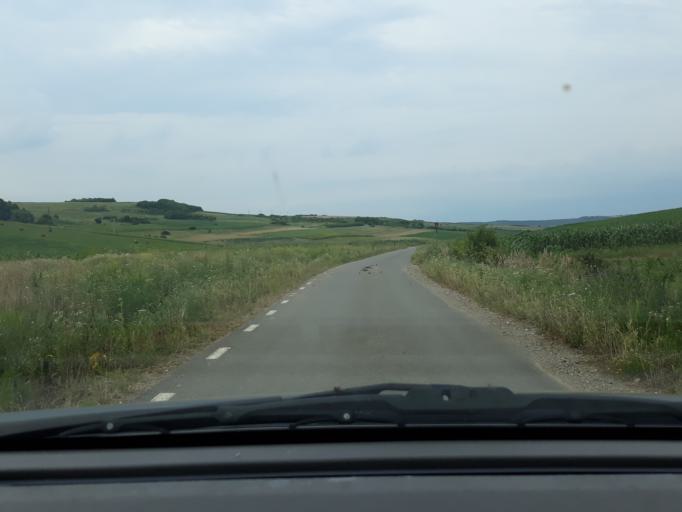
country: RO
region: Salaj
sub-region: Comuna Dobrin
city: Dobrin
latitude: 47.2845
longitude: 23.0939
